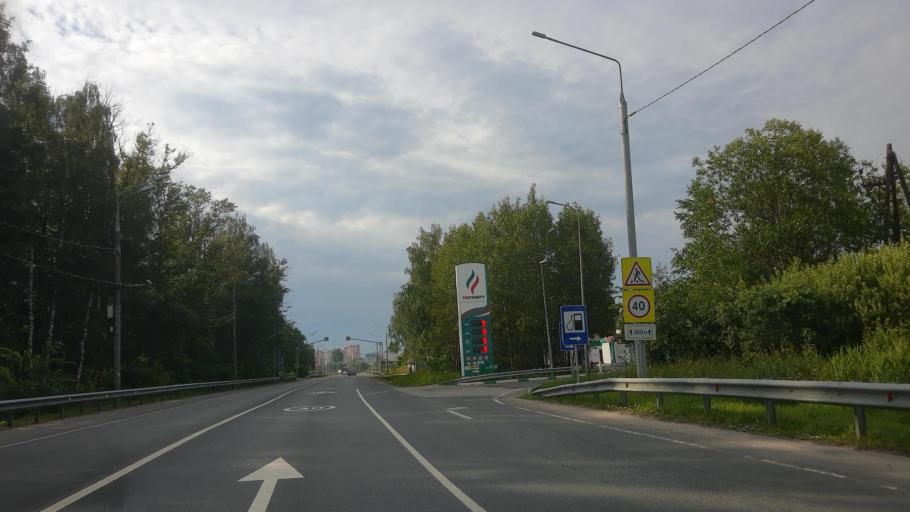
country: RU
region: Moskovskaya
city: Fryazevo
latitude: 55.7539
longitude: 38.4428
